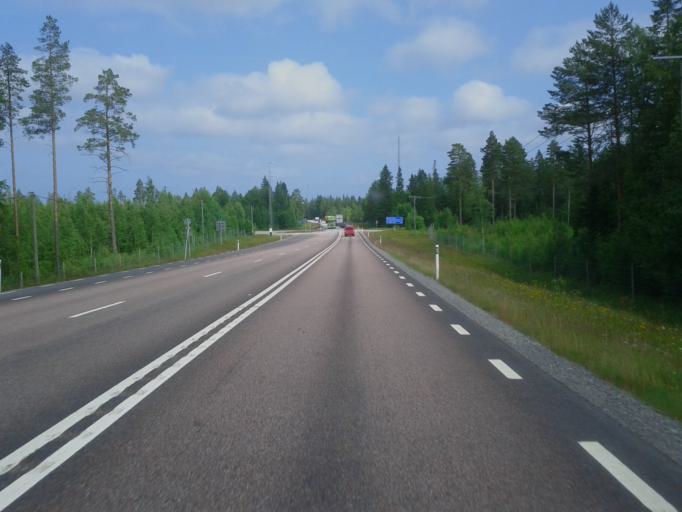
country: SE
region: Vaesterbotten
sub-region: Skelleftea Kommun
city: Burea
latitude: 64.4635
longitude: 21.2920
